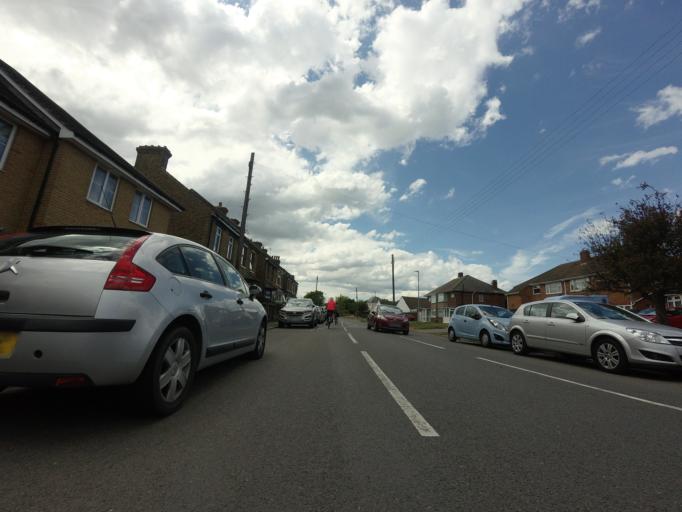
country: GB
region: England
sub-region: Kent
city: Hoo
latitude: 51.4203
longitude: 0.5589
